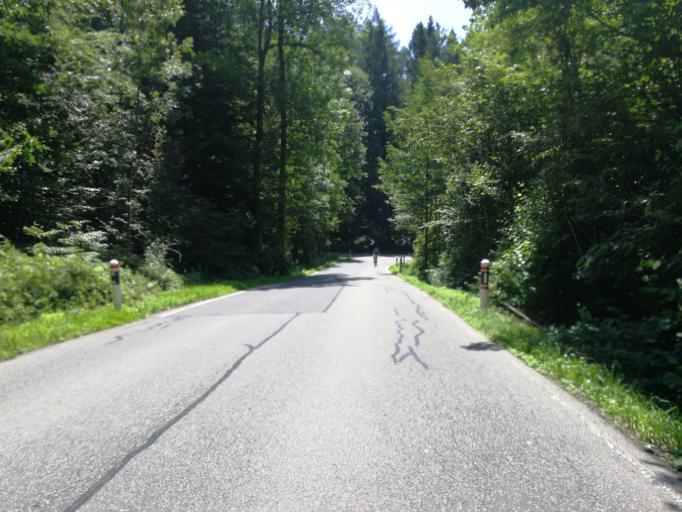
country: CH
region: Saint Gallen
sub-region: Wahlkreis See-Gaster
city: Eschenbach
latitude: 47.2295
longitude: 8.9229
